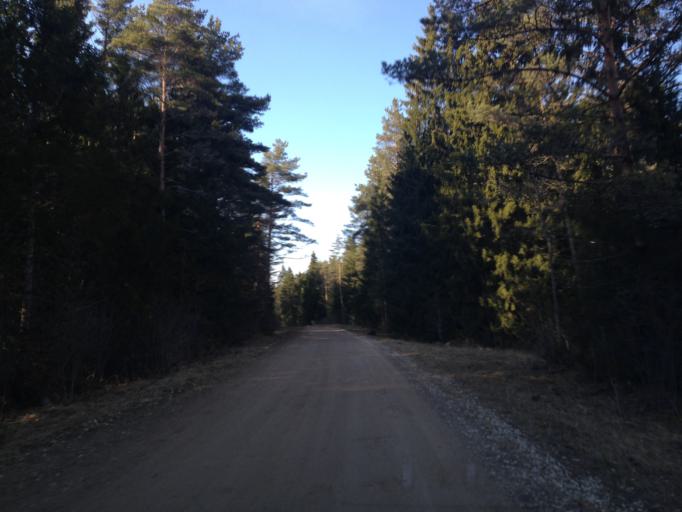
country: EE
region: Harju
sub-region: Nissi vald
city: Turba
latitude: 59.1080
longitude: 24.1574
